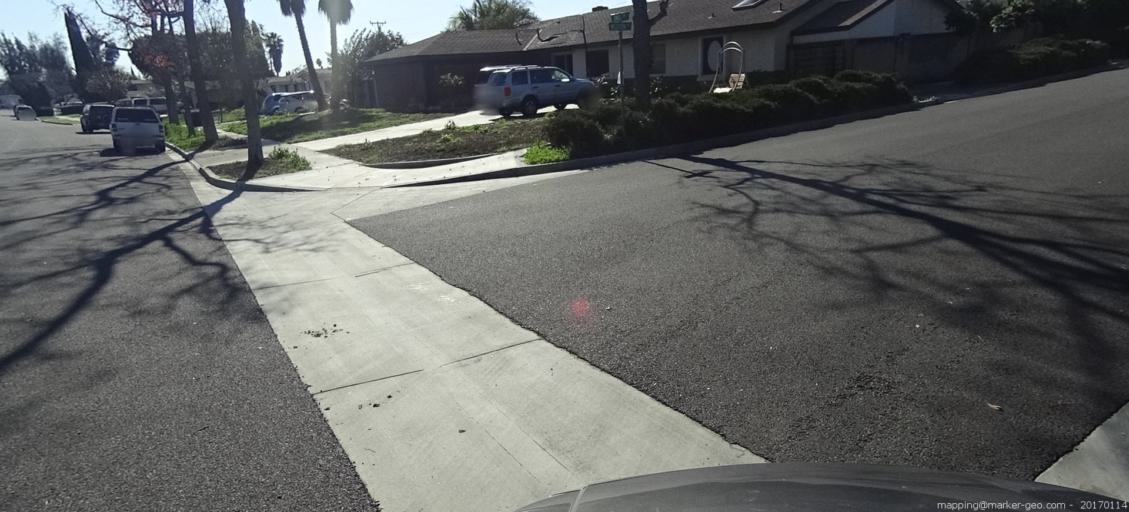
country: US
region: California
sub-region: Orange County
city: Tustin
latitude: 33.7585
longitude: -117.8160
